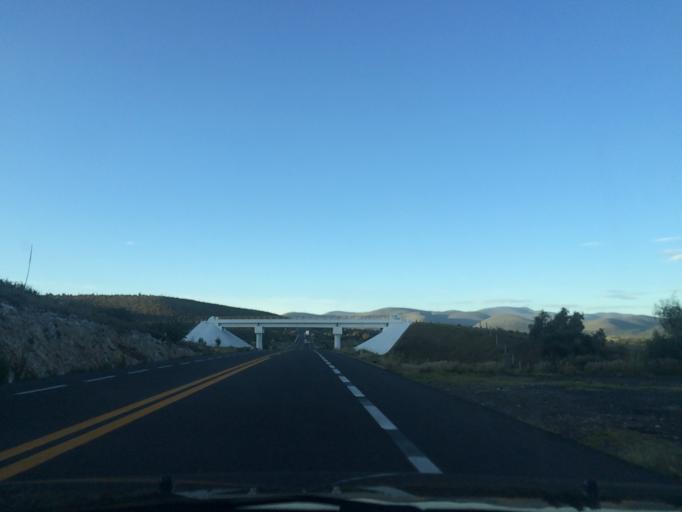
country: MX
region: Puebla
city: Cuacnopalan
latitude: 18.7959
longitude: -97.4894
